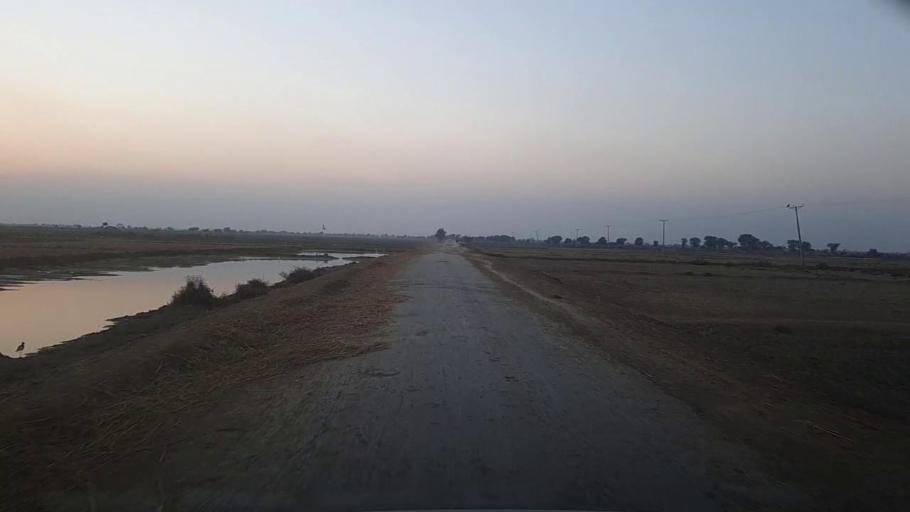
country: PK
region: Sindh
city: Khairpur Nathan Shah
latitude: 27.1801
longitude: 67.6144
